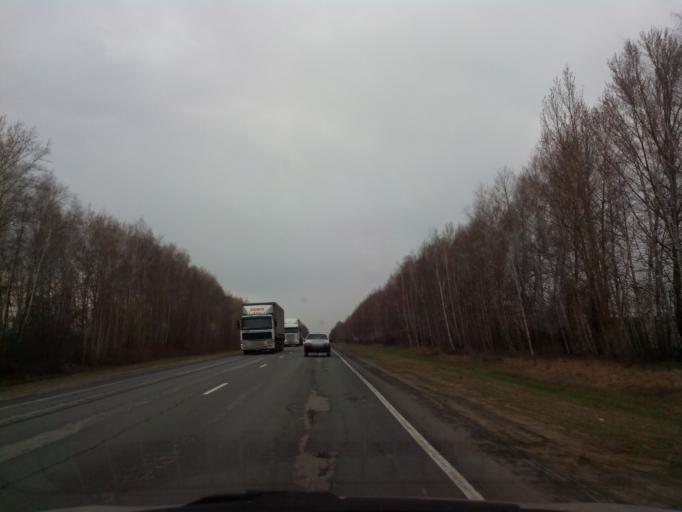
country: RU
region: Tambov
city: Michurinsk
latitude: 53.0678
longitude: 40.4367
